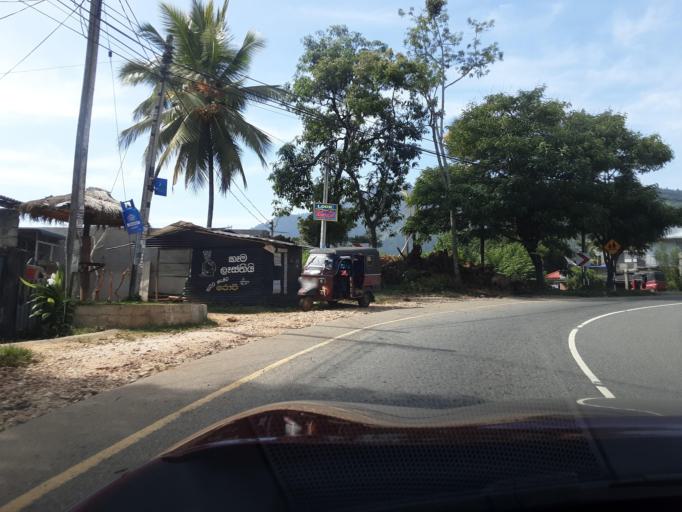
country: LK
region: Uva
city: Badulla
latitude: 6.9775
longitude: 81.0859
